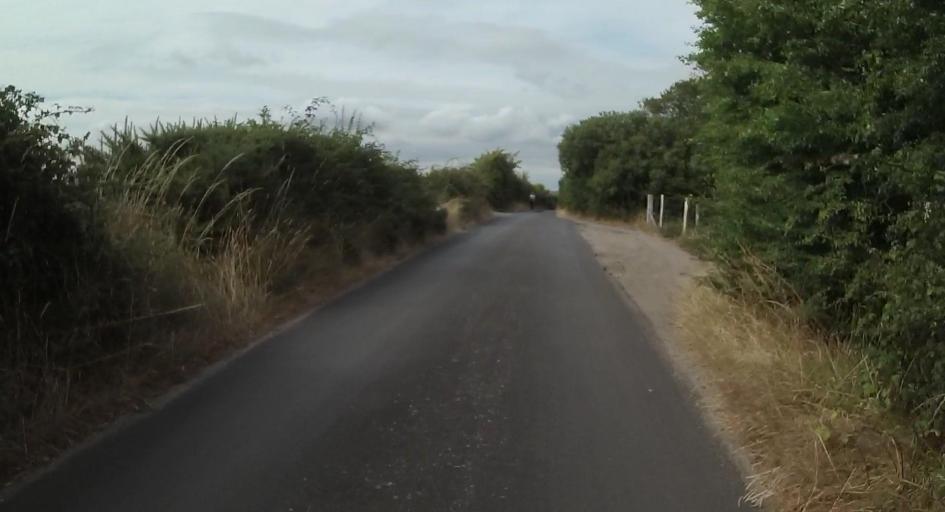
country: GB
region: England
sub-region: Dorset
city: Wareham
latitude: 50.6630
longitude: -2.0859
